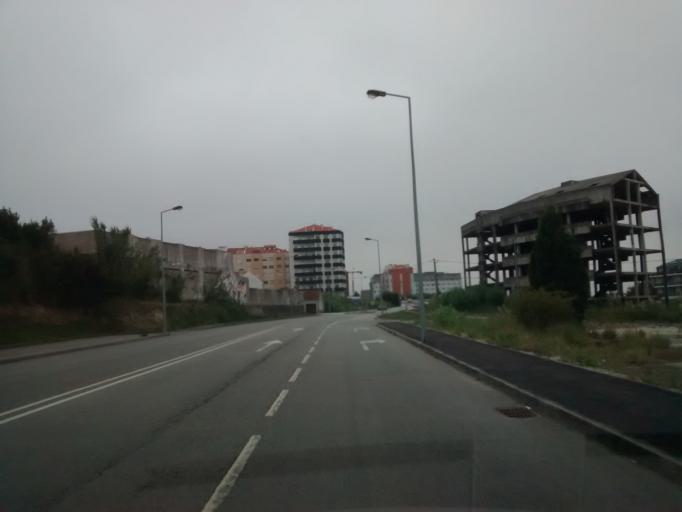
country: PT
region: Aveiro
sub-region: Aveiro
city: Aveiro
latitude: 40.6502
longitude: -8.6431
